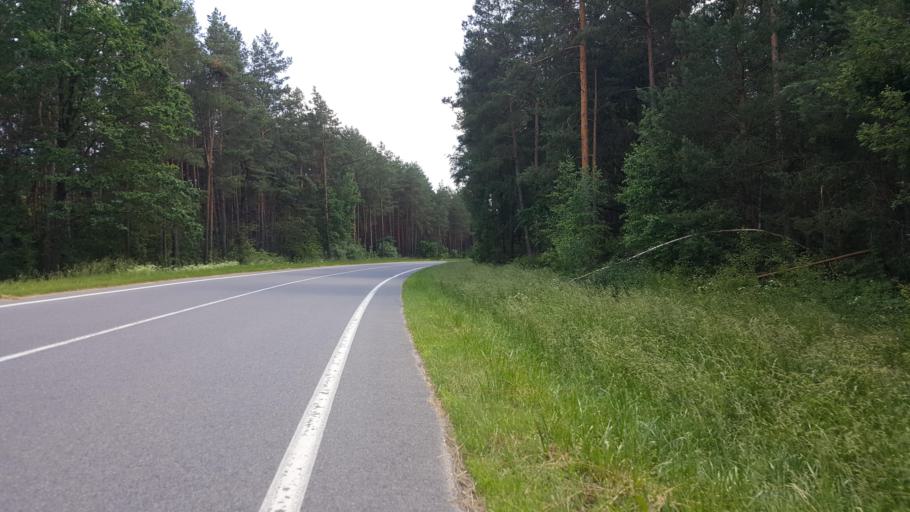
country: BY
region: Brest
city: Kamyanyuki
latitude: 52.5200
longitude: 23.6596
